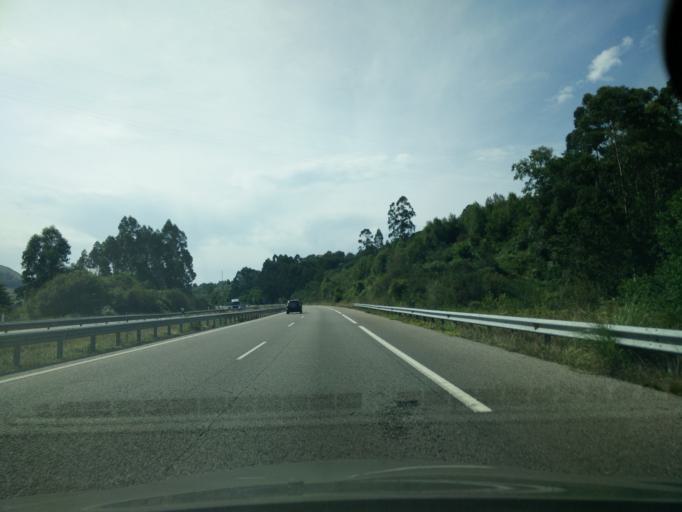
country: ES
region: Asturias
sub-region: Province of Asturias
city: Ribadesella
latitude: 43.4393
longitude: -5.0766
